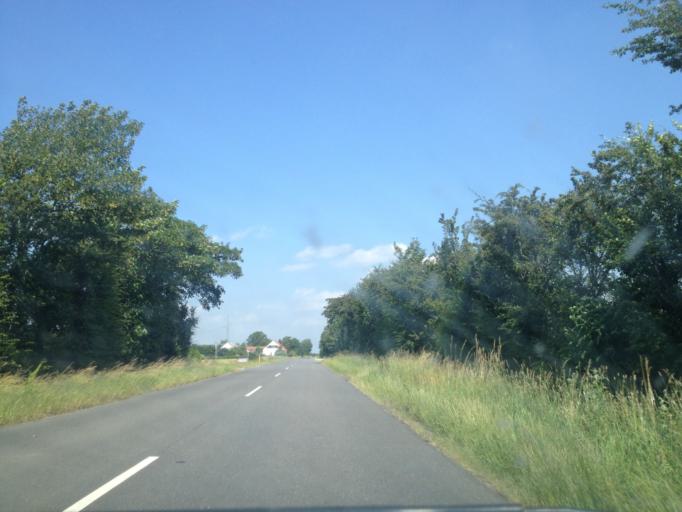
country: DK
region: South Denmark
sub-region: Kolding Kommune
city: Vamdrup
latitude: 55.4085
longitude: 9.2512
